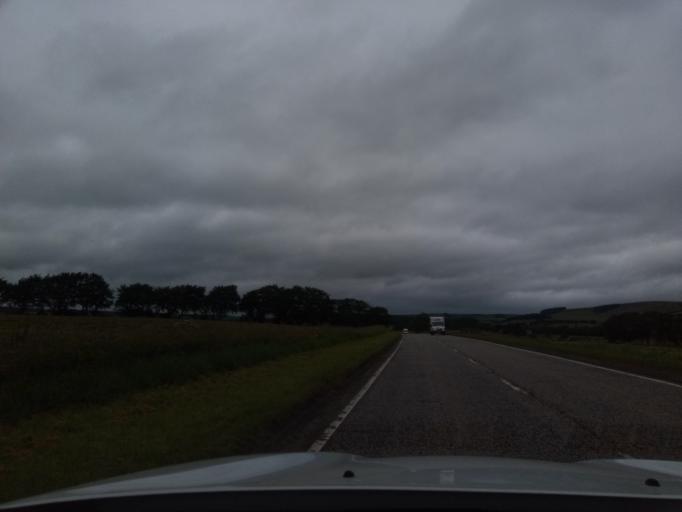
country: GB
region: Scotland
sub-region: The Scottish Borders
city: Lauder
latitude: 55.7503
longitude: -2.7731
